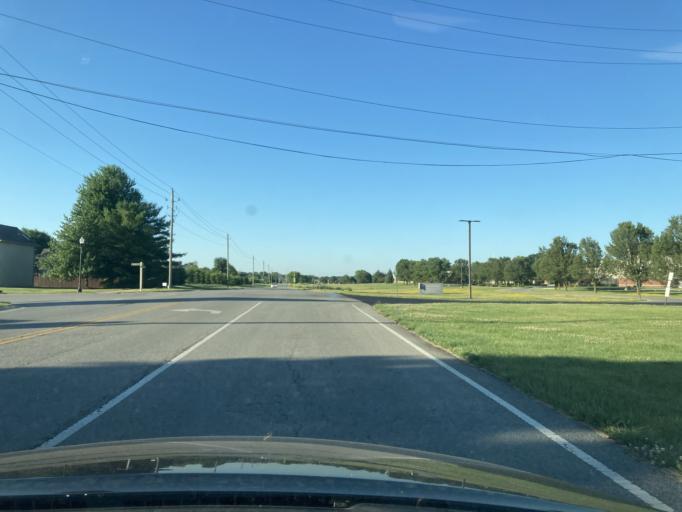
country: US
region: Indiana
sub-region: Marion County
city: Meridian Hills
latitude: 39.8763
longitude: -86.2222
